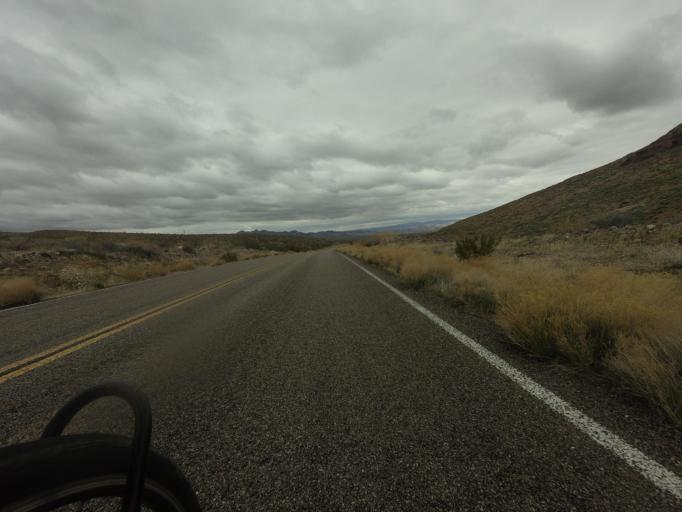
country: US
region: Nevada
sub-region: Nye County
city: Beatty
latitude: 36.8051
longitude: -116.9159
